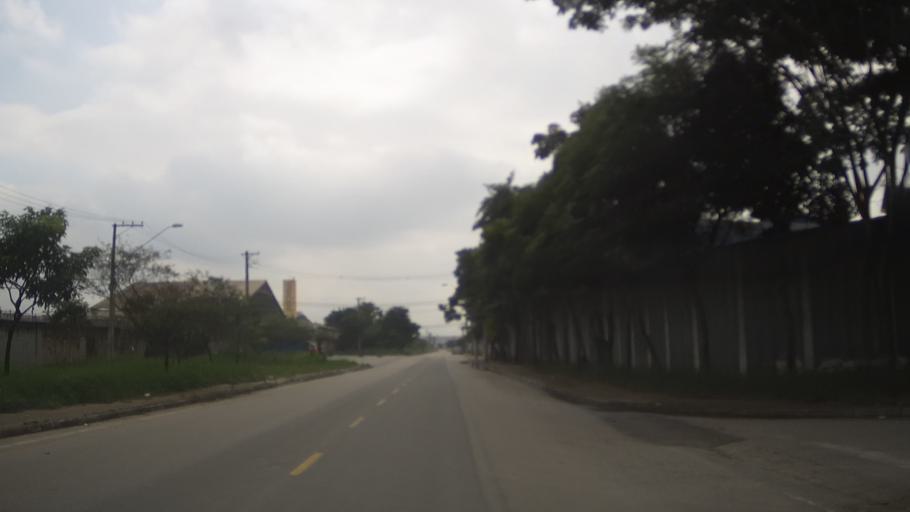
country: BR
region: Sao Paulo
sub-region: Guarulhos
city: Guarulhos
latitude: -23.4678
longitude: -46.4704
